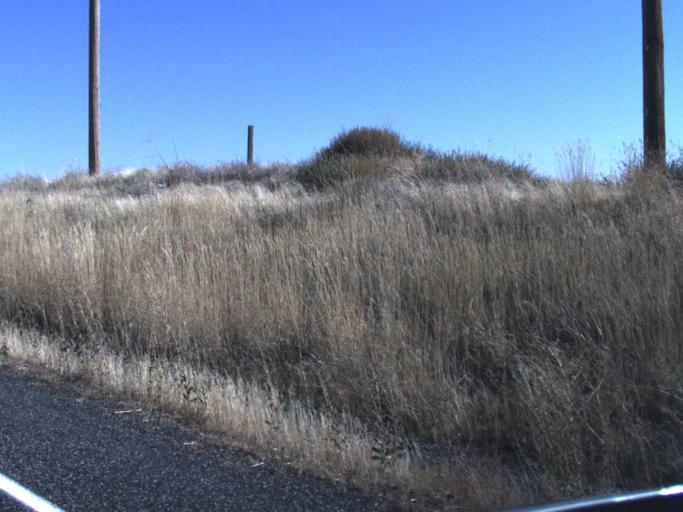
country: US
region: Washington
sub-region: Walla Walla County
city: Burbank
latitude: 46.2741
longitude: -118.7653
